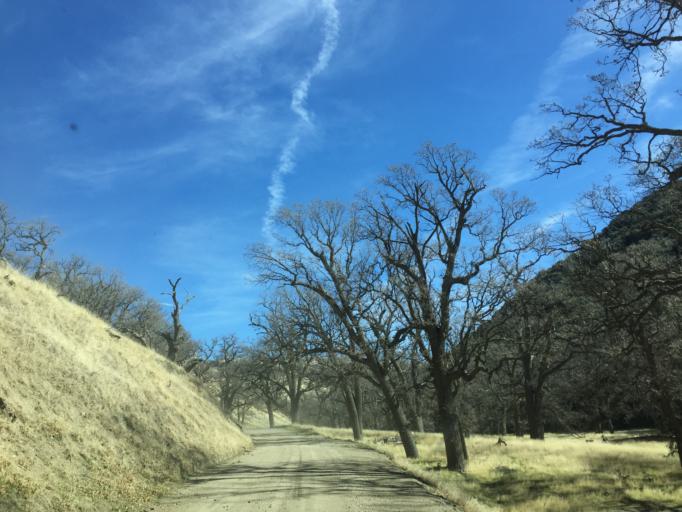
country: US
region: California
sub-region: Kern County
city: Lebec
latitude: 34.9128
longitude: -118.6995
